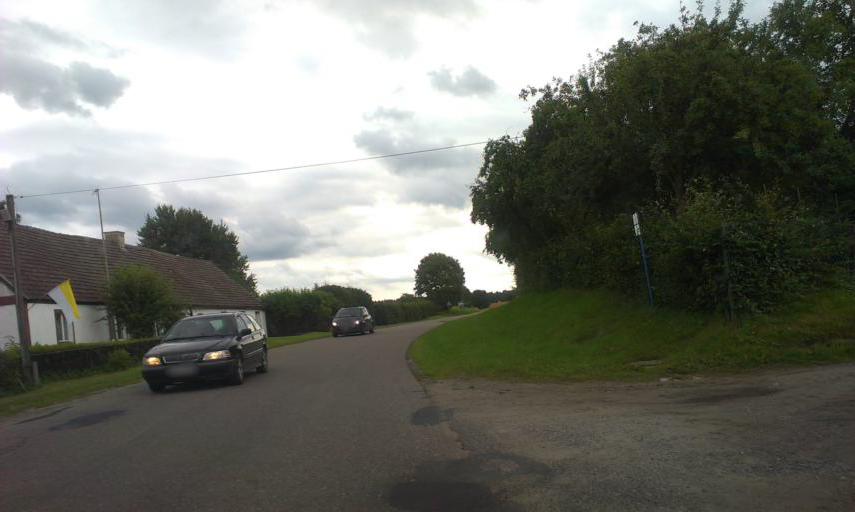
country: PL
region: West Pomeranian Voivodeship
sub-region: Powiat bialogardzki
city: Tychowo
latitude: 53.9705
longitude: 16.2098
